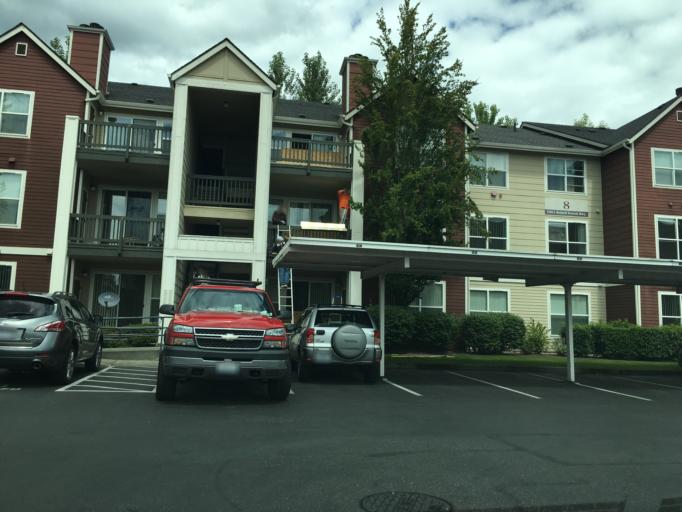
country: US
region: Washington
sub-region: Snohomish County
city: North Creek
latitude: 47.8179
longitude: -122.2071
